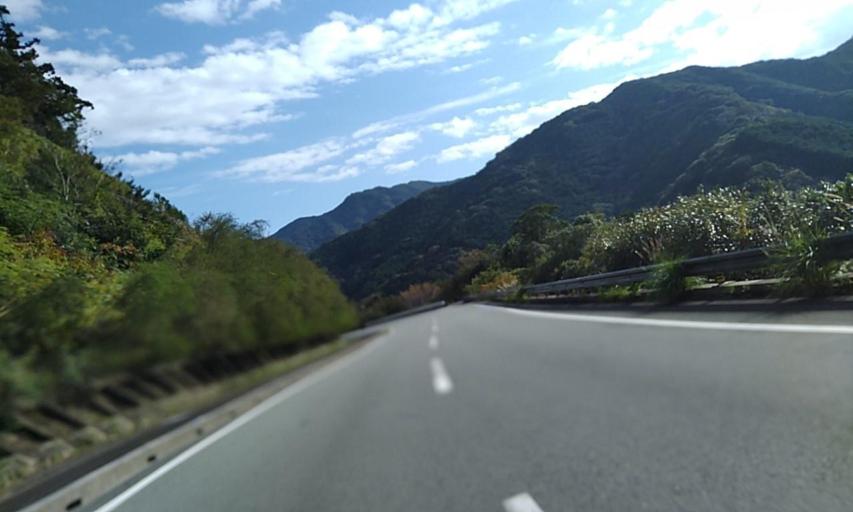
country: JP
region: Mie
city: Owase
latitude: 34.2524
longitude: 136.4305
